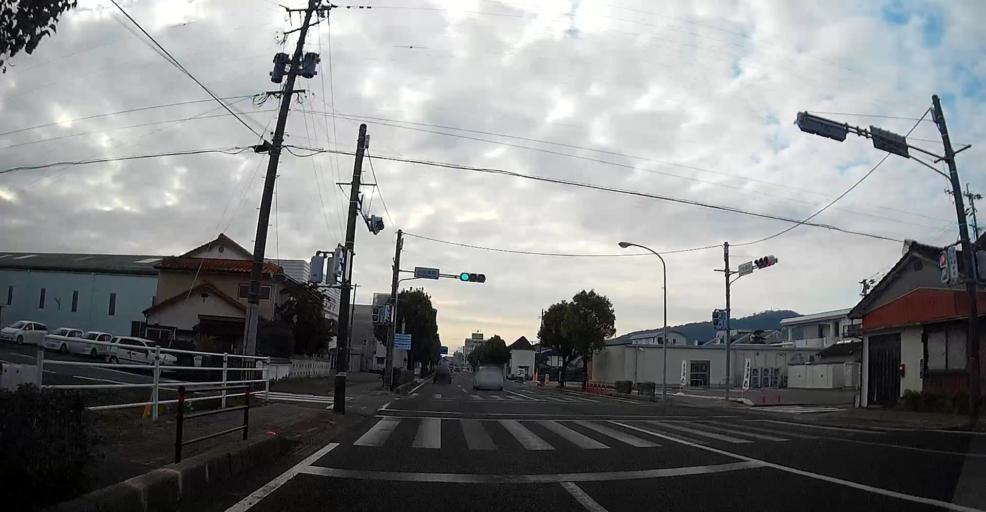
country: JP
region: Kumamoto
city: Hondo
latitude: 32.4616
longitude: 130.1913
